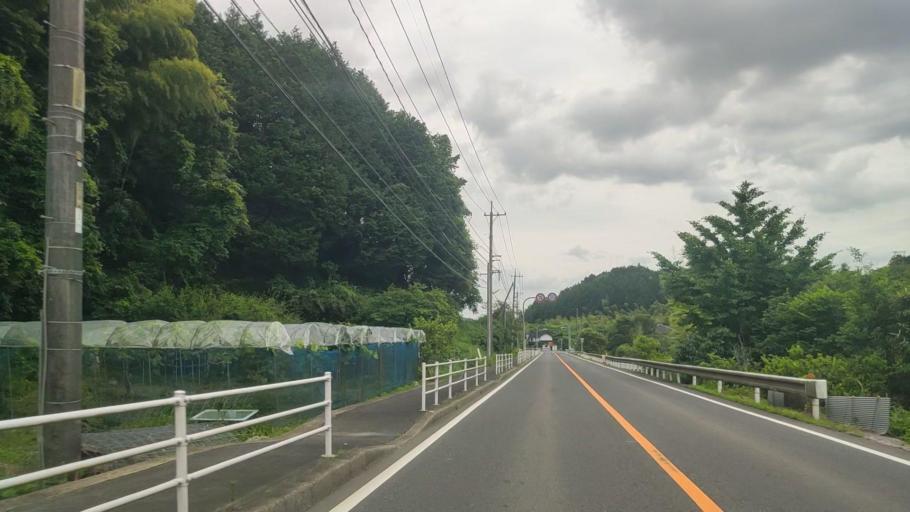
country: JP
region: Okayama
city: Tsuyama
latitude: 35.0622
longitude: 133.8350
